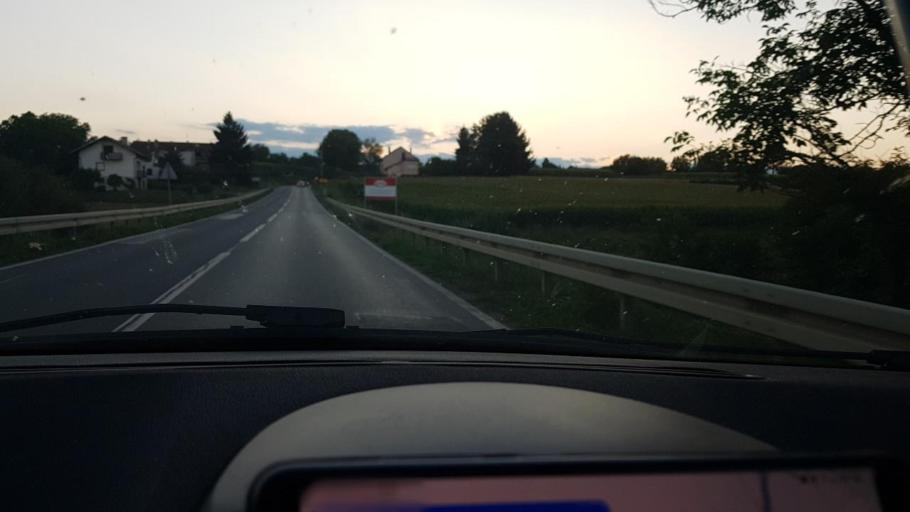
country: HR
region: Bjelovarsko-Bilogorska
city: Zdralovi
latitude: 45.8750
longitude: 16.8846
